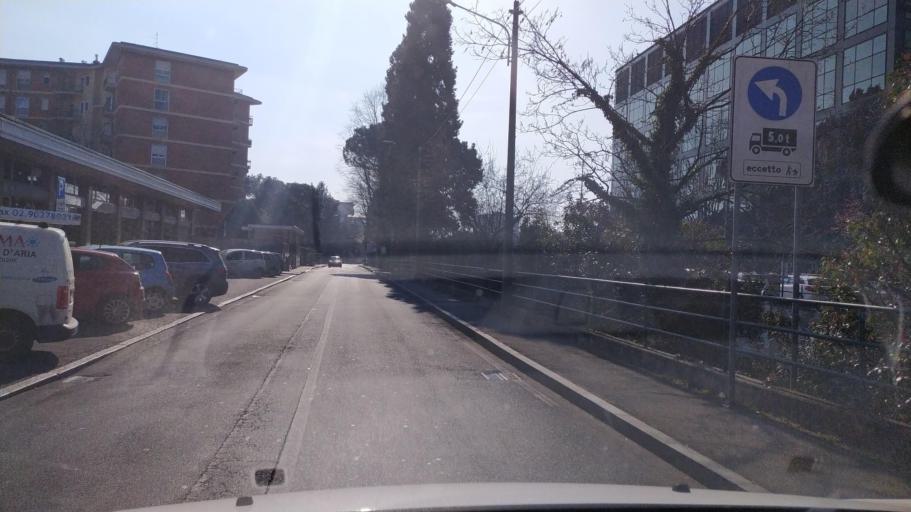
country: IT
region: Lombardy
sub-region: Provincia di Varese
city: Gallarate
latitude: 45.6656
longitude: 8.7969
